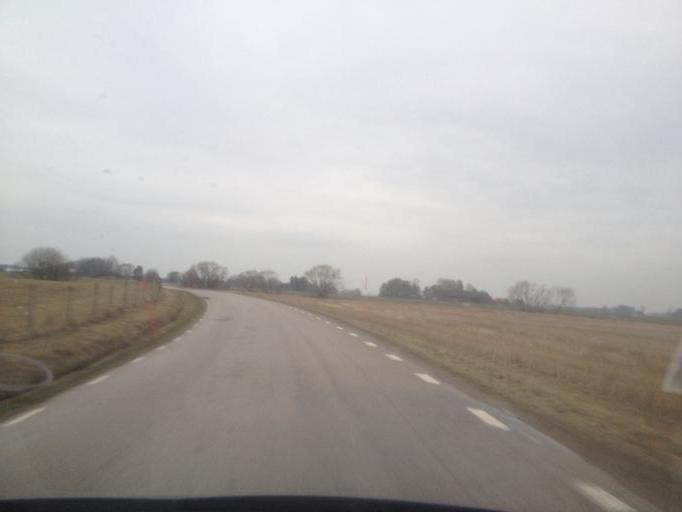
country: SE
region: OEstergoetland
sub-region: Linkopings Kommun
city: Vikingstad
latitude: 58.4206
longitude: 15.4351
